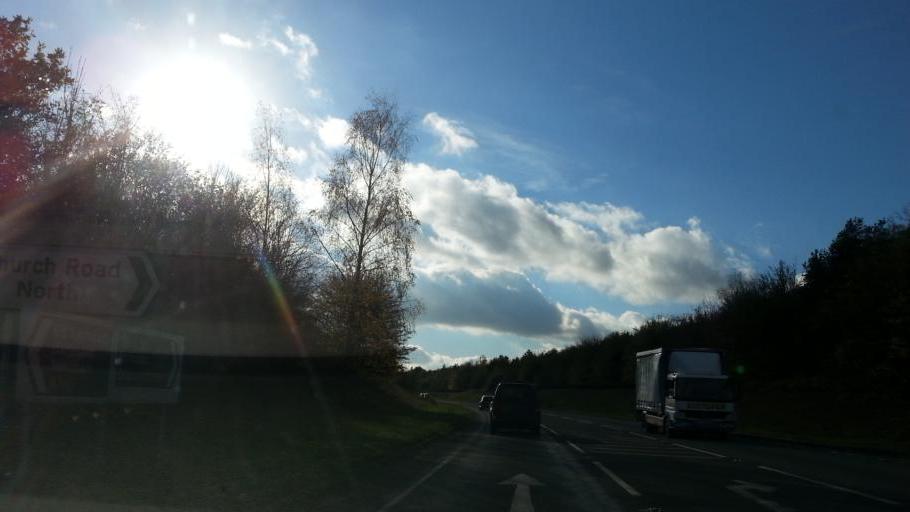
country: GB
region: England
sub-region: Norfolk
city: Harleston
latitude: 52.3728
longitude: 1.2382
